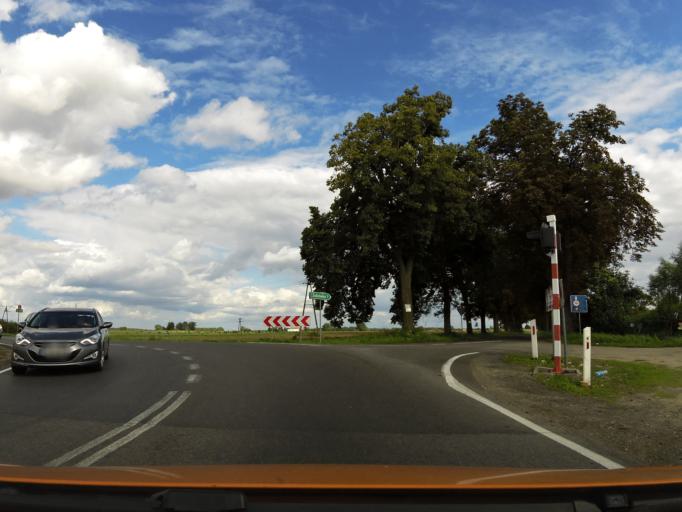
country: PL
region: West Pomeranian Voivodeship
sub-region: Powiat goleniowski
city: Nowogard
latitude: 53.7256
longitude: 15.1968
